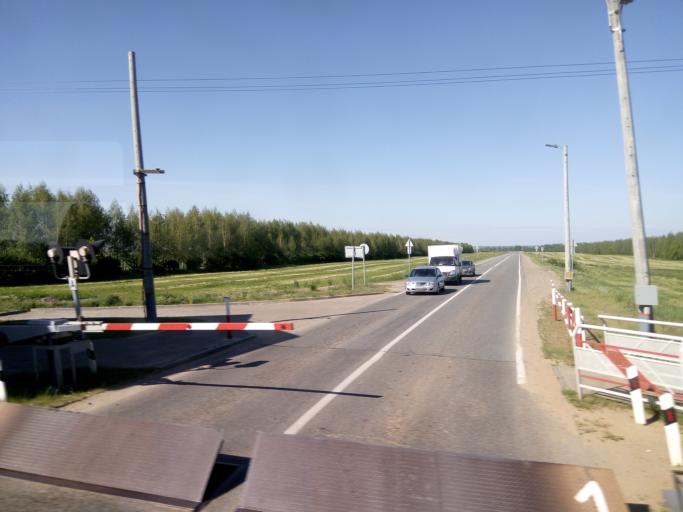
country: RU
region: Tatarstan
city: Stolbishchi
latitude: 55.6319
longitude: 49.2502
